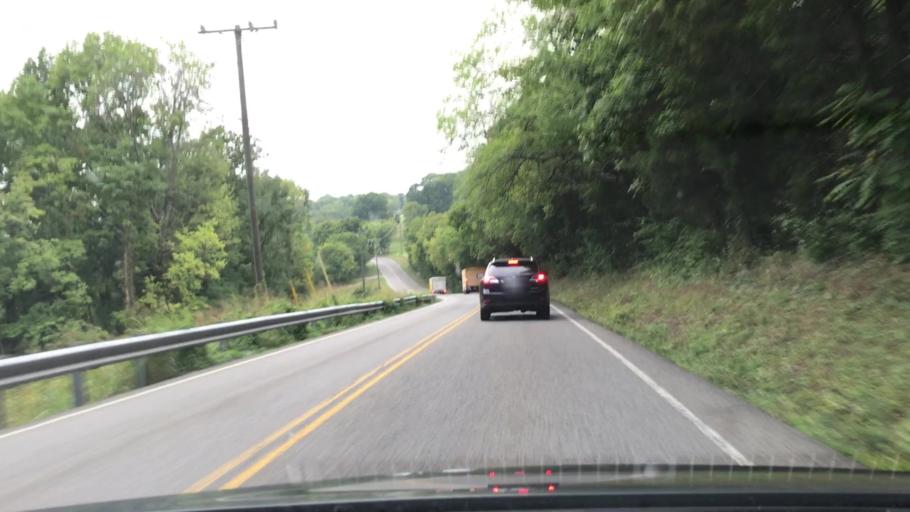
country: US
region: Tennessee
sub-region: Williamson County
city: Nolensville
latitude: 35.9272
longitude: -86.7191
